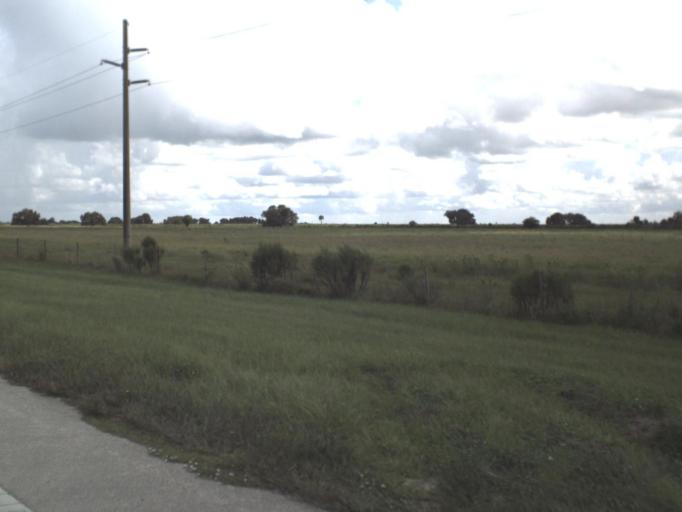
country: US
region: Florida
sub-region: DeSoto County
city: Southeast Arcadia
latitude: 27.2095
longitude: -81.6427
